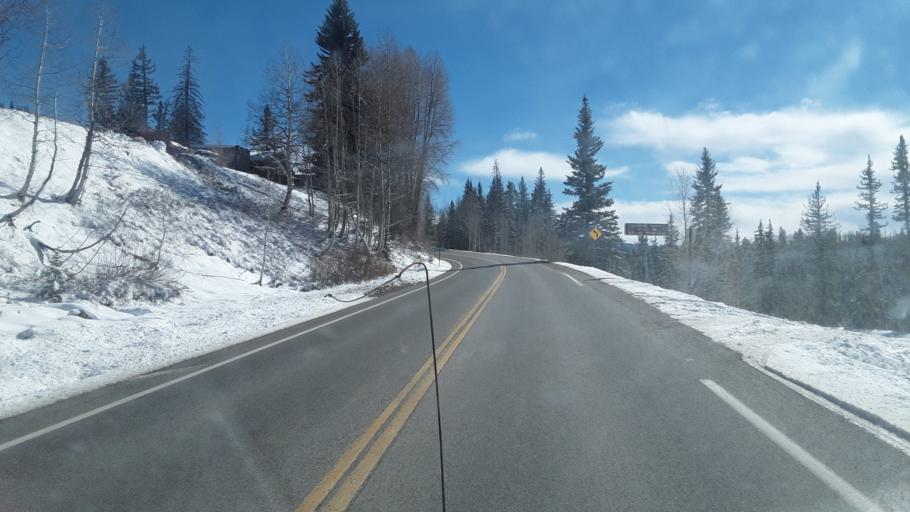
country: US
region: Colorado
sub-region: San Juan County
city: Silverton
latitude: 37.6586
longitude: -107.8096
